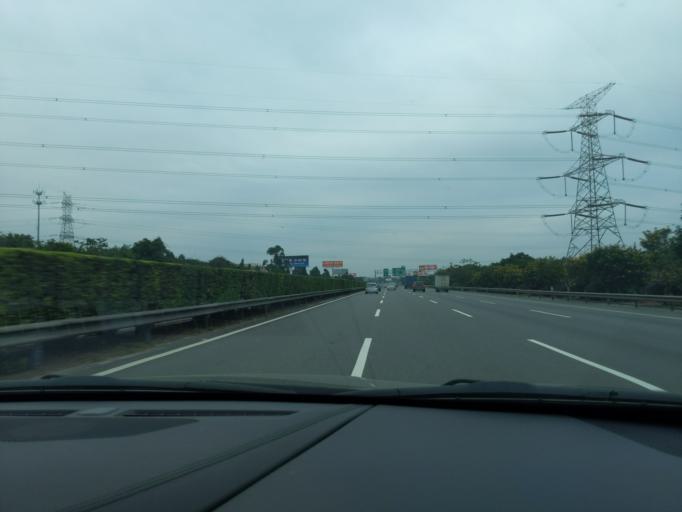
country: CN
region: Fujian
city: Neikeng
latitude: 24.7597
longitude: 118.4471
